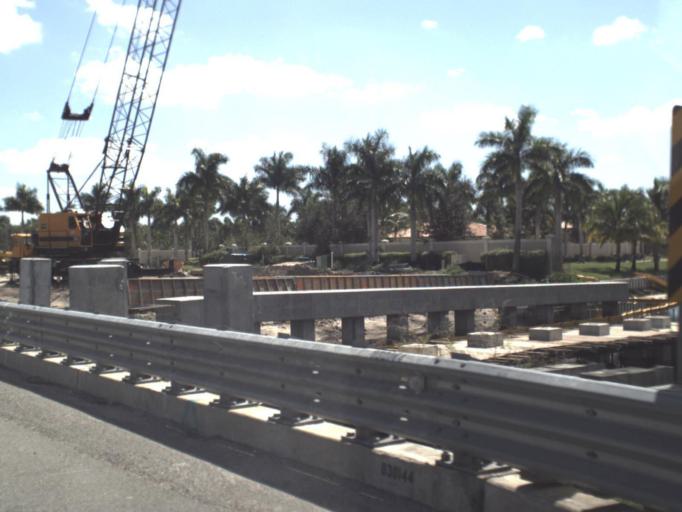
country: US
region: Florida
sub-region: Collier County
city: Lely Resort
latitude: 26.0574
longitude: -81.6899
